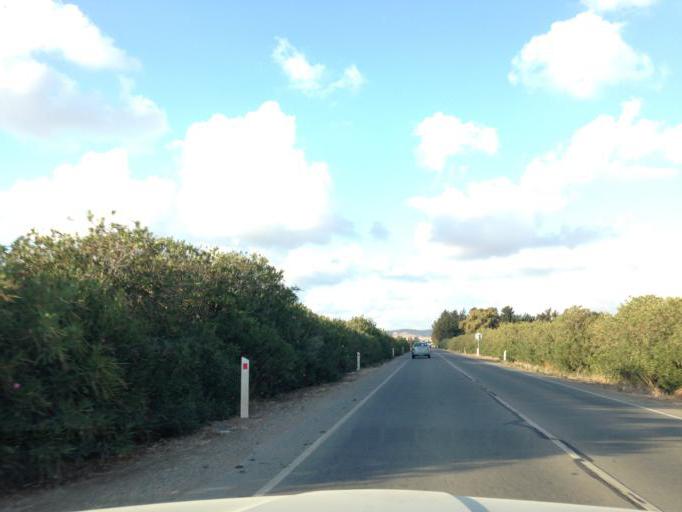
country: CY
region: Pafos
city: Paphos
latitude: 34.7147
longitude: 32.5125
